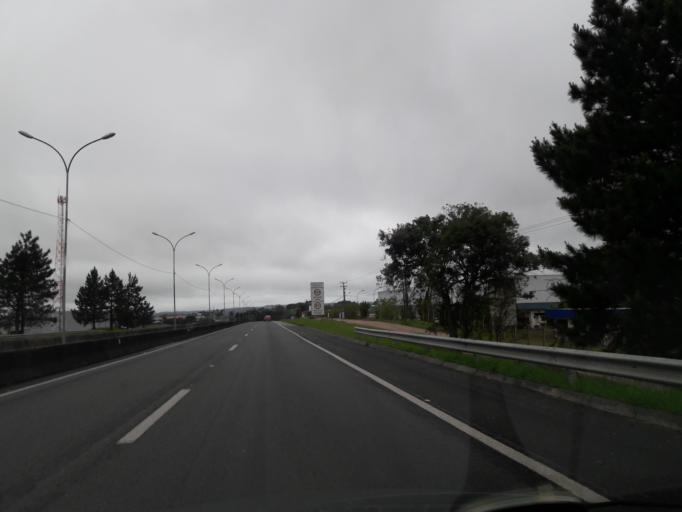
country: BR
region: Parana
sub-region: Quatro Barras
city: Quatro Barras
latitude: -25.3585
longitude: -49.0727
